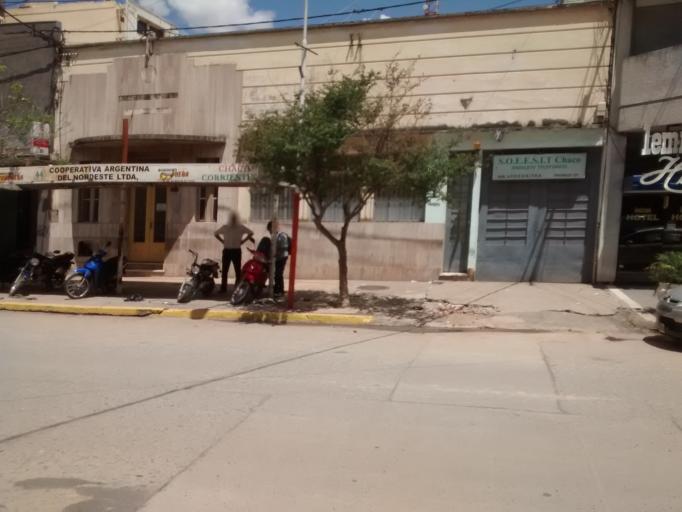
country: AR
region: Chaco
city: Resistencia
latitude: -27.4532
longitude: -58.9871
